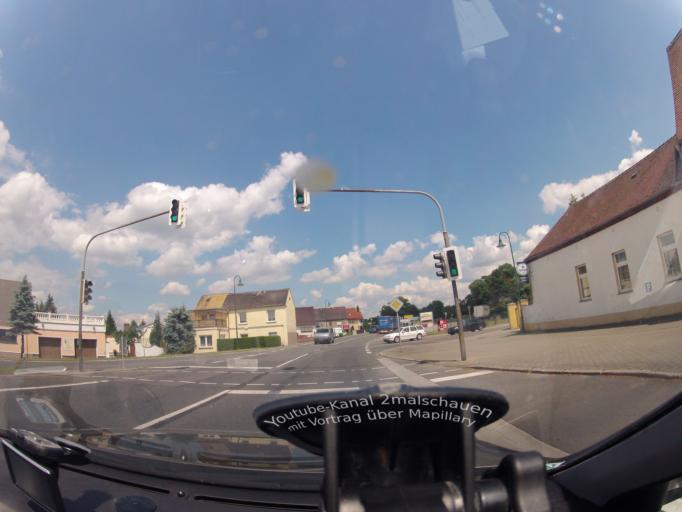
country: DE
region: Saxony
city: Doberschutz
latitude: 51.4986
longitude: 12.7485
